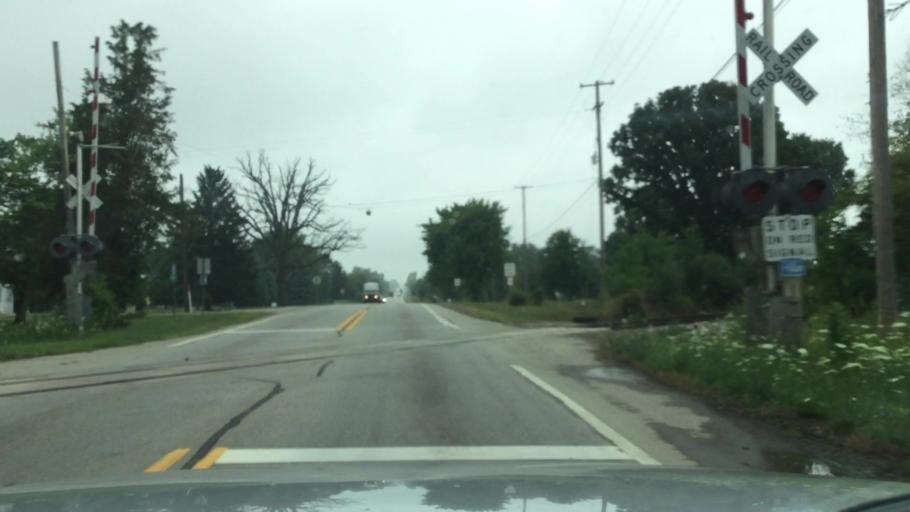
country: US
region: Michigan
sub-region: Shiawassee County
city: Durand
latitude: 42.9870
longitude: -83.9287
